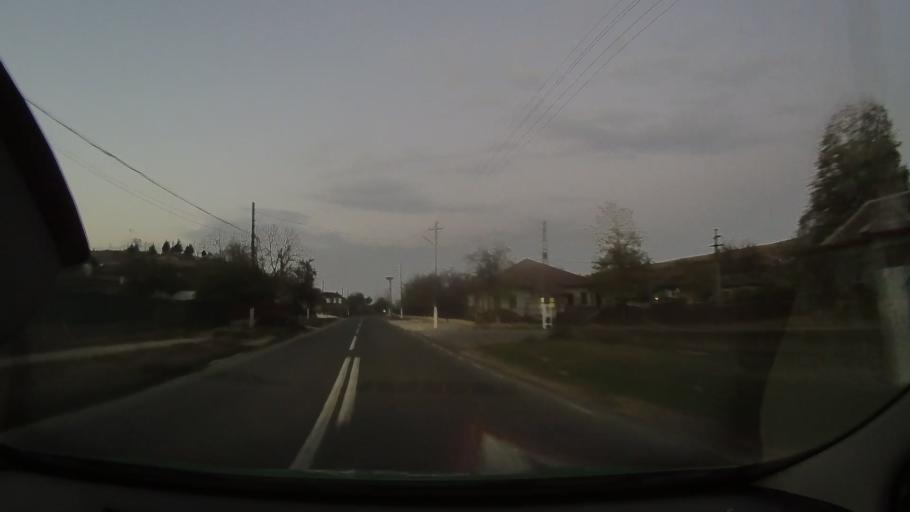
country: RO
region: Constanta
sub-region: Comuna Ion Corvin
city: Ion Corvin
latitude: 44.0966
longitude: 27.7548
